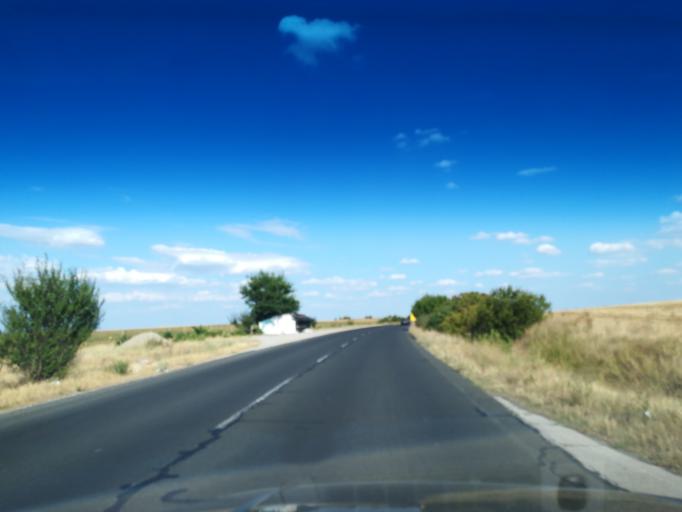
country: BG
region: Stara Zagora
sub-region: Obshtina Chirpan
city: Chirpan
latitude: 42.0590
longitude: 25.2800
